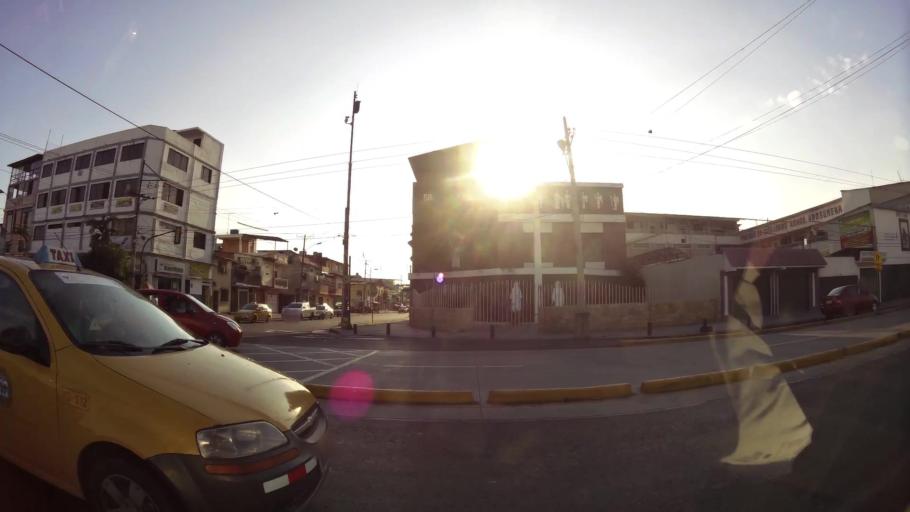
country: EC
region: Guayas
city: Guayaquil
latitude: -2.2186
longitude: -79.8984
